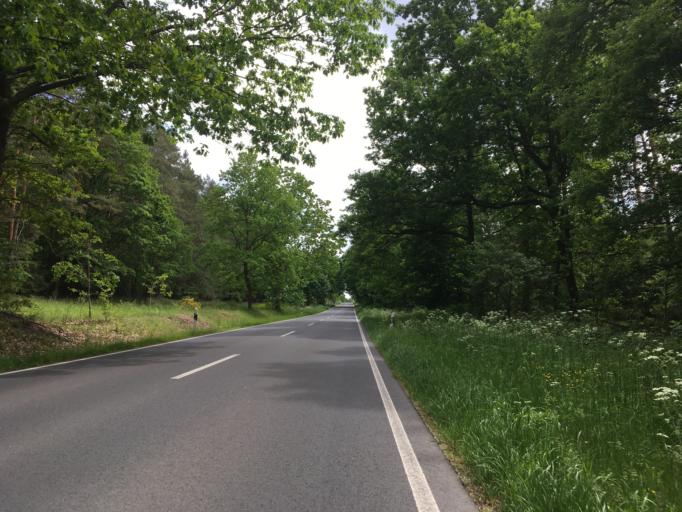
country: DE
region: Brandenburg
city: Falkenberg
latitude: 52.7616
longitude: 13.9696
